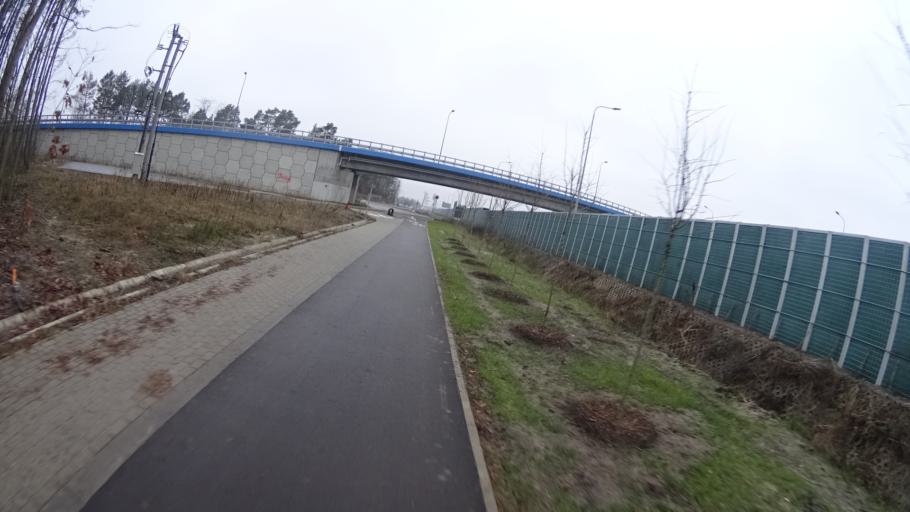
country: PL
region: Masovian Voivodeship
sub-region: Warszawa
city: Wawer
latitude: 52.1661
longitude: 21.1875
